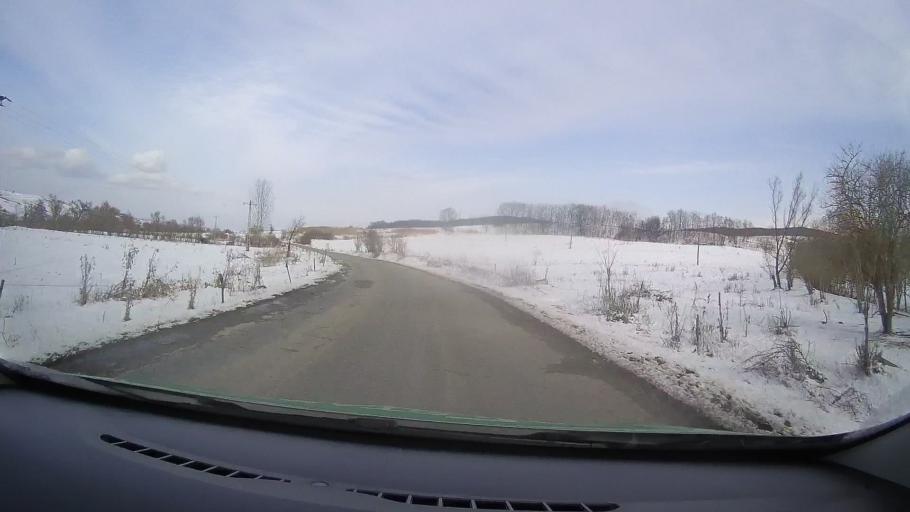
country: RO
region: Sibiu
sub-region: Oras Agnita
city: Ruja
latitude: 45.9840
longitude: 24.6558
